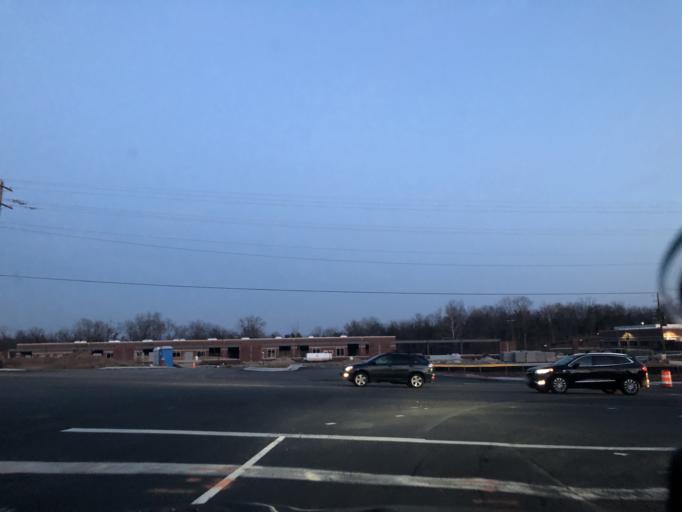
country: US
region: Virginia
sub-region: Loudoun County
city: Leesburg
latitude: 39.0804
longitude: -77.5535
